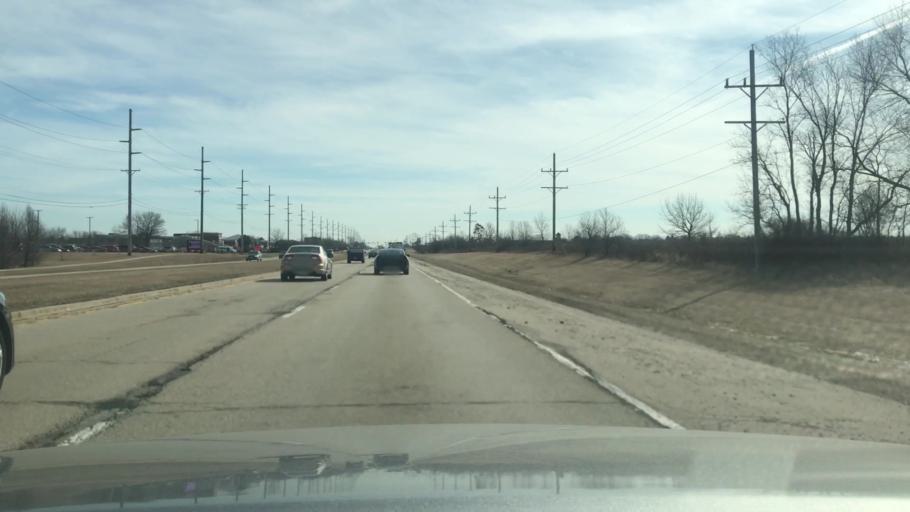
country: US
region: Illinois
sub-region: DuPage County
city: Naperville
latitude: 41.7474
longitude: -88.1774
